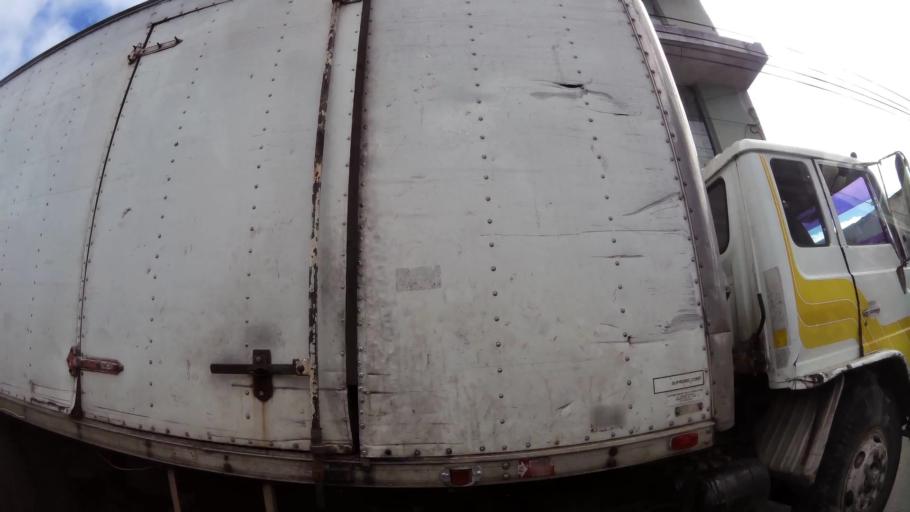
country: GT
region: Guatemala
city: Guatemala City
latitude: 14.6412
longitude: -90.5532
